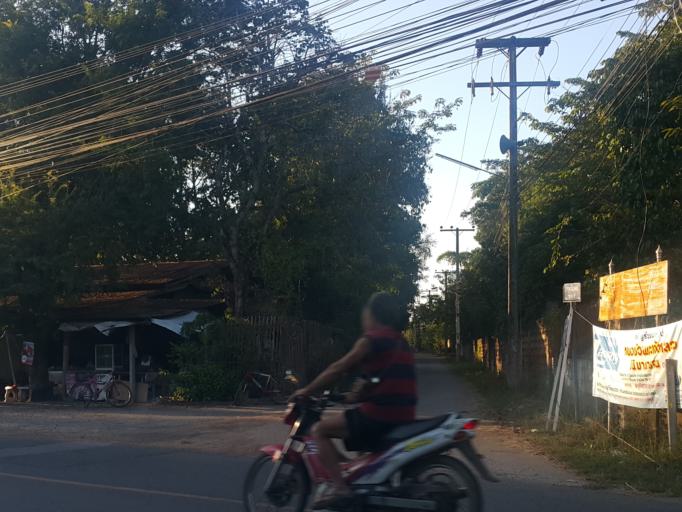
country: TH
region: Chiang Mai
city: San Sai
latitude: 18.8752
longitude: 99.1510
